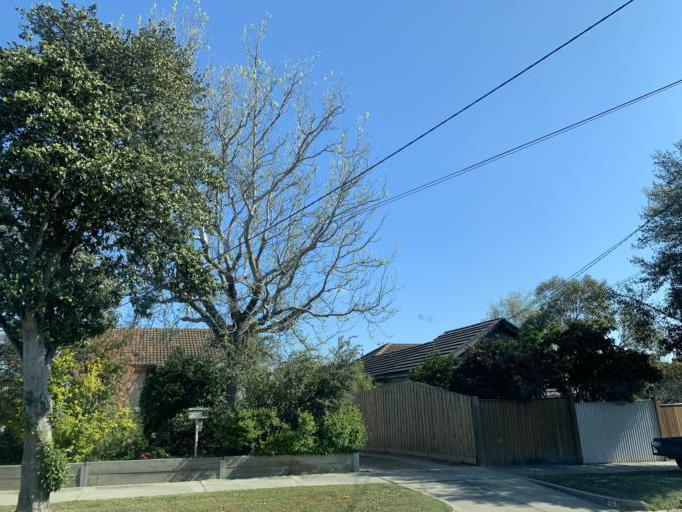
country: AU
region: Victoria
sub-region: Kingston
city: Mordialloc
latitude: -37.9962
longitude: 145.0873
